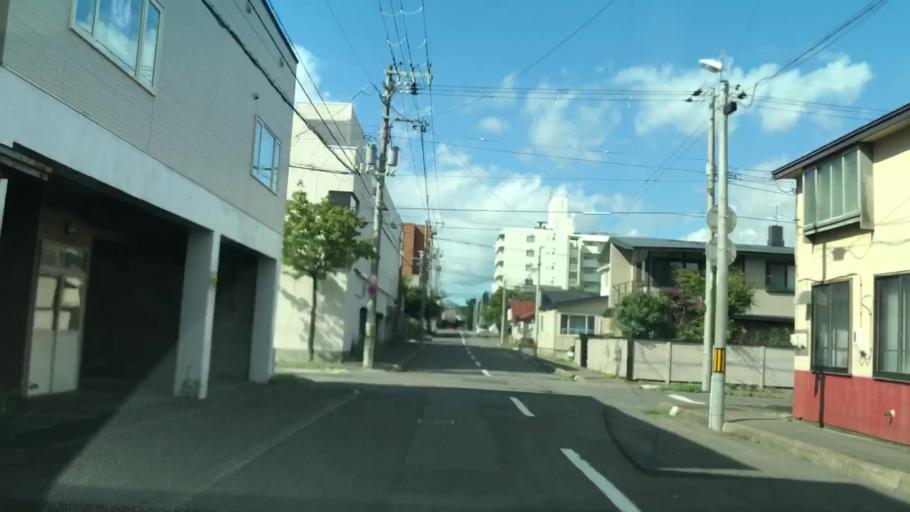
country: JP
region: Hokkaido
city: Muroran
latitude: 42.3140
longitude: 140.9712
